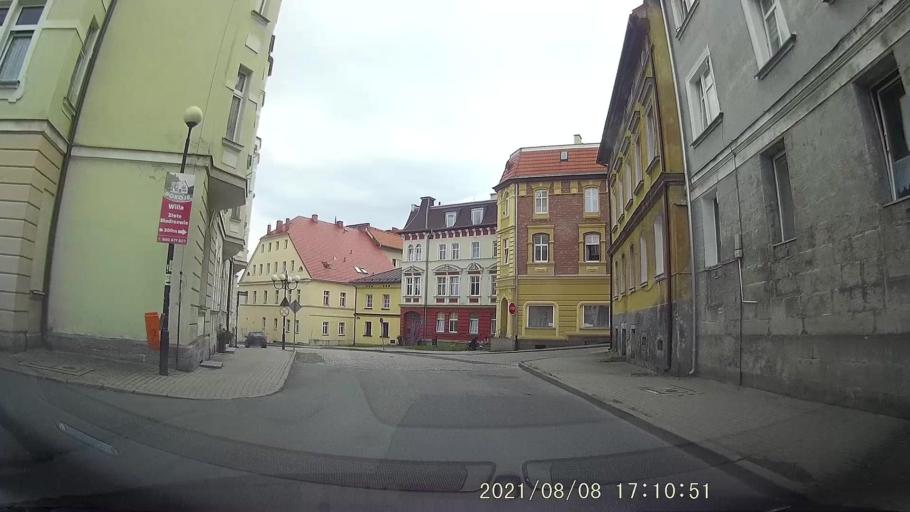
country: PL
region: Lower Silesian Voivodeship
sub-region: Powiat klodzki
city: Duszniki-Zdroj
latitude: 50.4048
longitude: 16.3883
